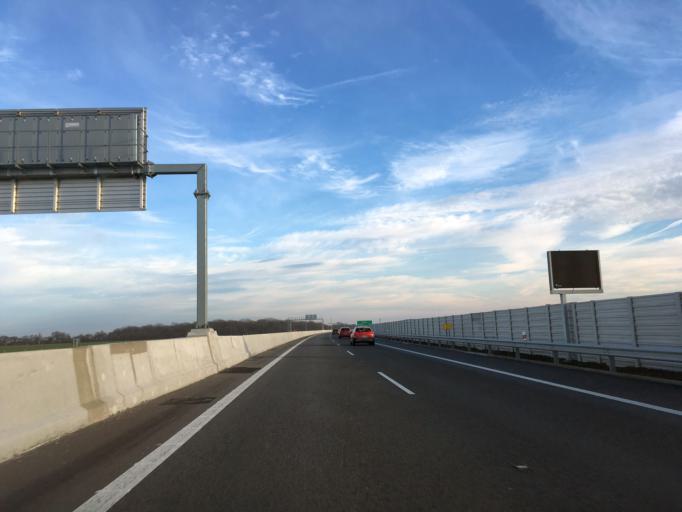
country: SK
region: Bratislavsky
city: Dunajska Luzna
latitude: 48.0869
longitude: 17.2114
